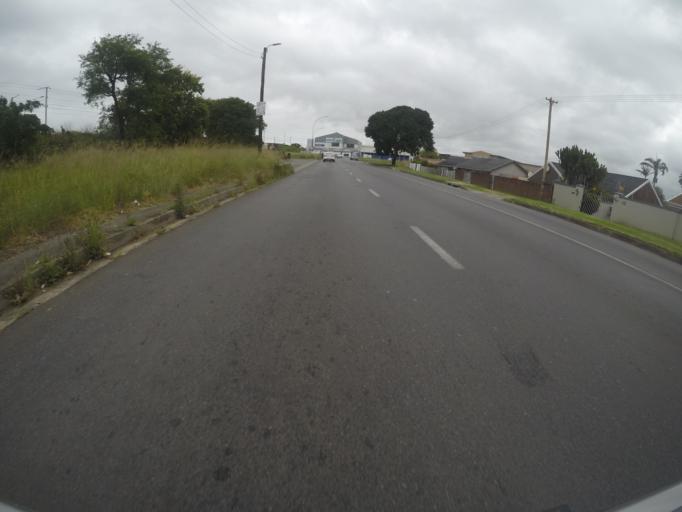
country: ZA
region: Eastern Cape
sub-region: Buffalo City Metropolitan Municipality
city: East London
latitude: -32.9828
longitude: 27.8971
